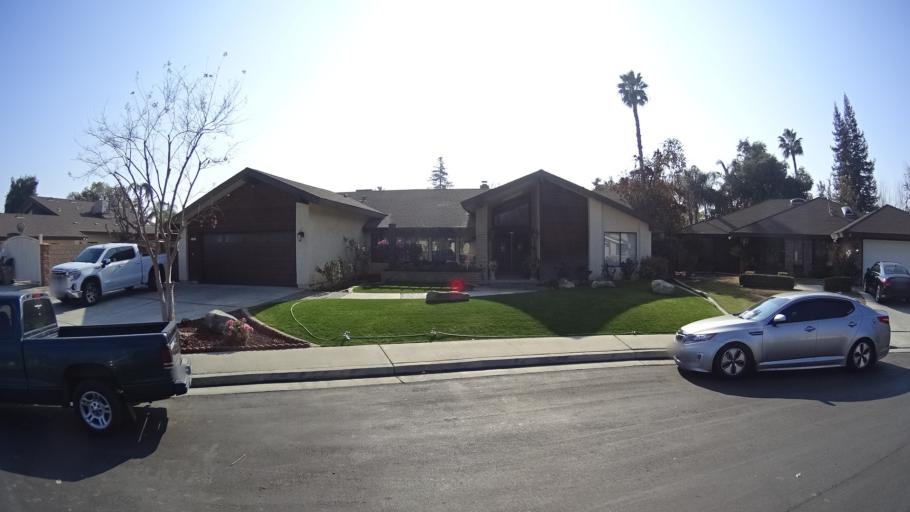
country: US
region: California
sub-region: Kern County
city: Greenacres
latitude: 35.3300
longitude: -119.0822
